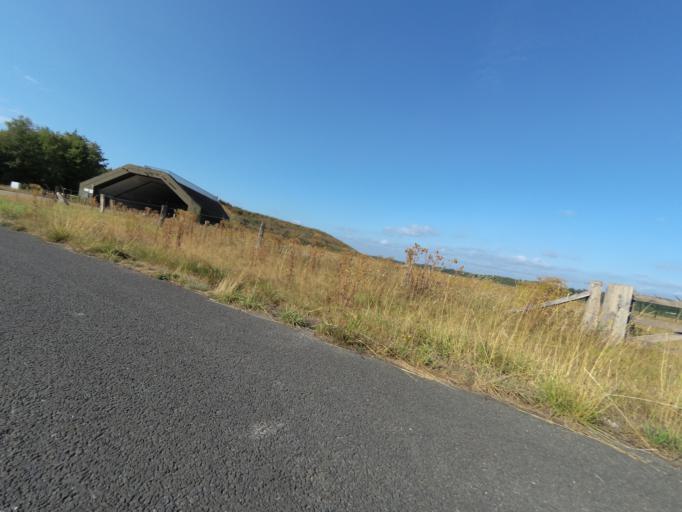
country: NL
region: Overijssel
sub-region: Gemeente Oldenzaal
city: Oldenzaal
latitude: 52.2781
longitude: 6.9004
